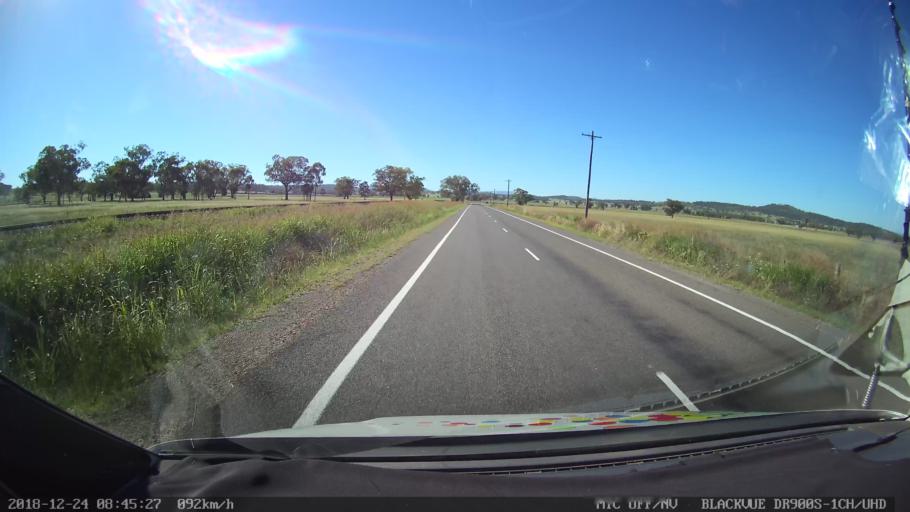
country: AU
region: New South Wales
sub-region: Liverpool Plains
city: Quirindi
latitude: -31.4152
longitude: 150.6521
